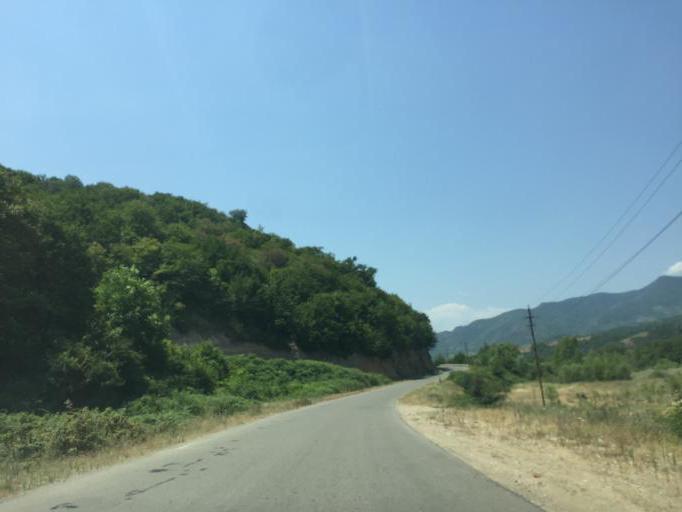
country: AZ
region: Tartar Rayon
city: Martakert
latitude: 40.1331
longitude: 46.4790
